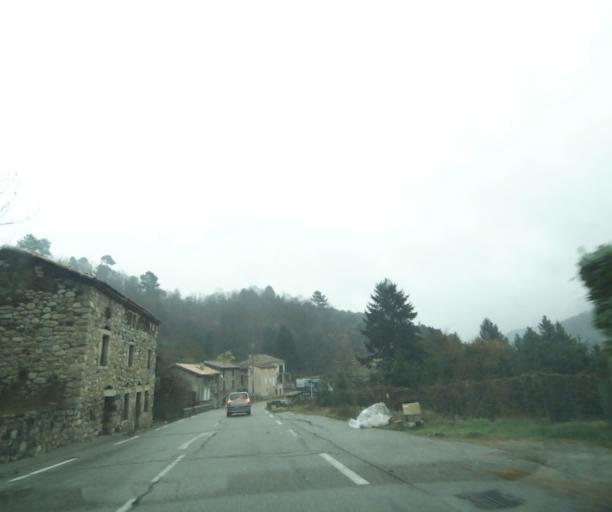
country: FR
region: Rhone-Alpes
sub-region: Departement de l'Ardeche
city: Thueyts
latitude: 44.6778
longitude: 4.2388
